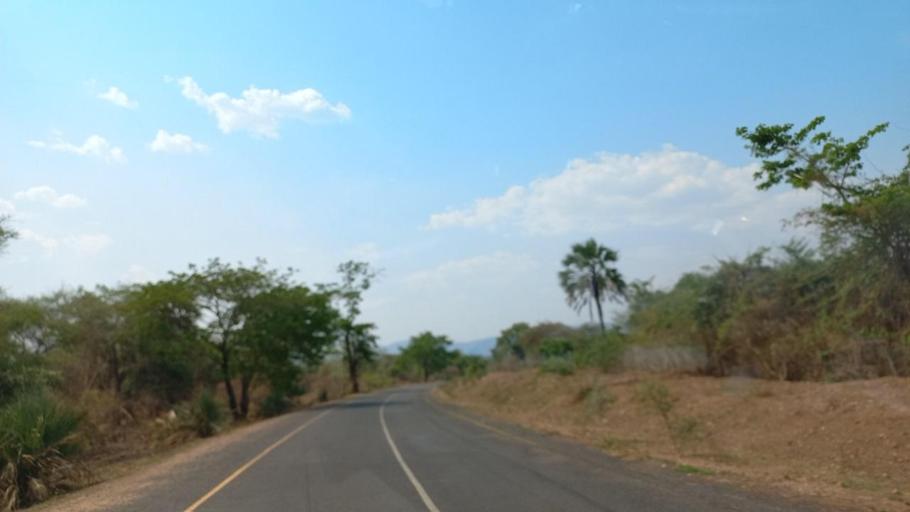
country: ZM
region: Lusaka
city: Luangwa
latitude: -15.1011
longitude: 30.1940
